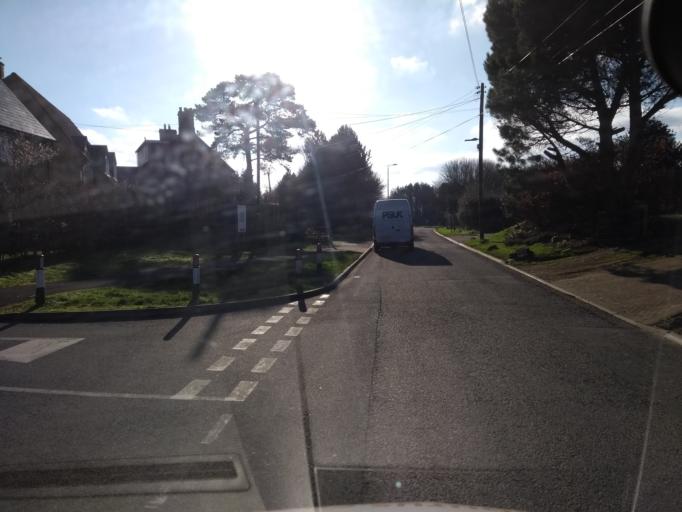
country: GB
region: England
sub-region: Somerset
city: South Petherton
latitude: 50.9437
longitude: -2.8029
